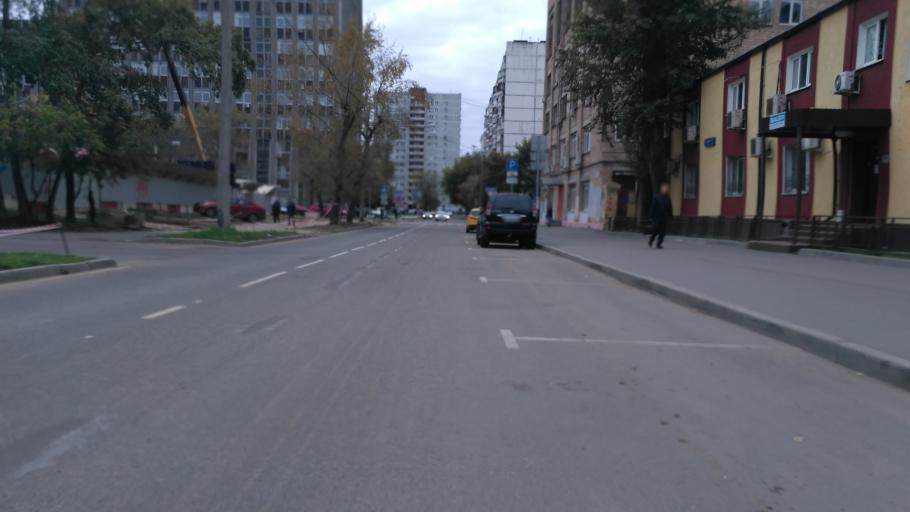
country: RU
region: Moscow
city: Mar'ina Roshcha
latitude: 55.7991
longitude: 37.6082
